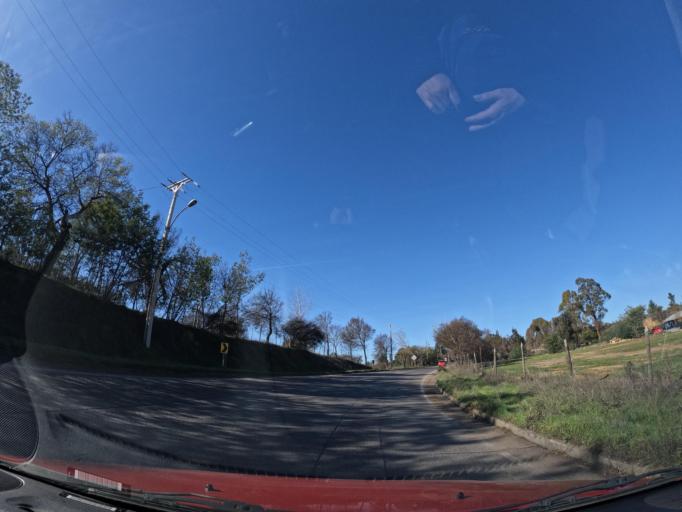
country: CL
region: Maule
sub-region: Provincia de Cauquenes
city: Cauquenes
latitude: -35.9553
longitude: -72.3102
